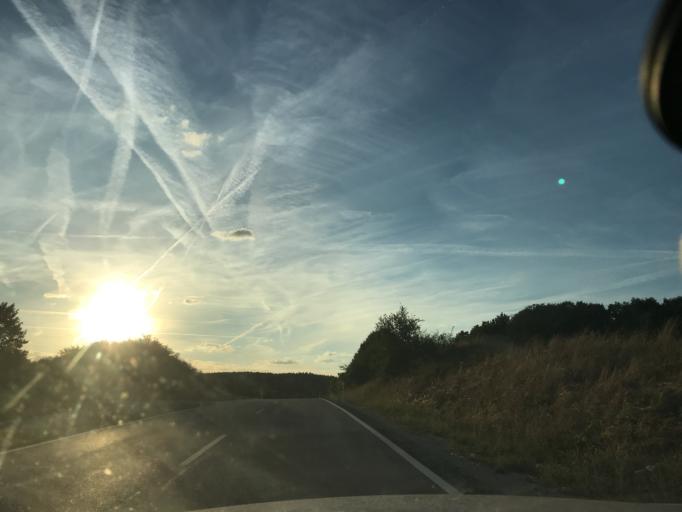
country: DE
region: Bavaria
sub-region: Upper Franconia
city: Pegnitz
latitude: 49.7212
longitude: 11.5690
